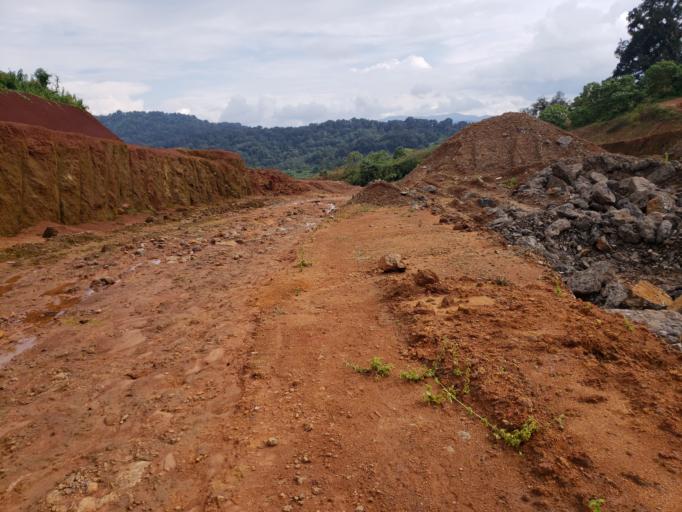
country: ET
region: Oromiya
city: Dodola
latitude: 6.5452
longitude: 39.4219
